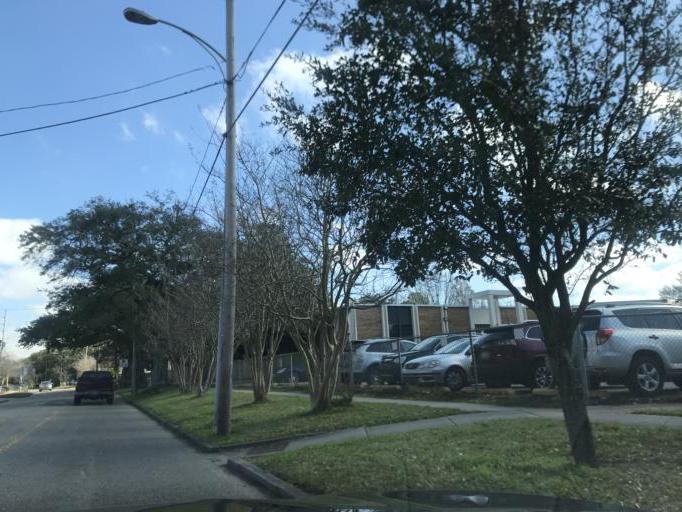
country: US
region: Louisiana
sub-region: Jefferson Parish
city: Metairie
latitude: 29.9867
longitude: -90.1406
